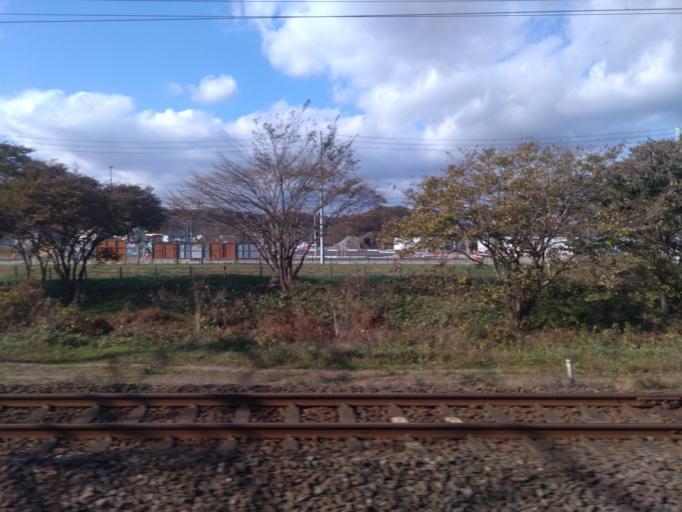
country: JP
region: Hokkaido
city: Shiraoi
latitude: 42.5576
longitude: 141.3643
